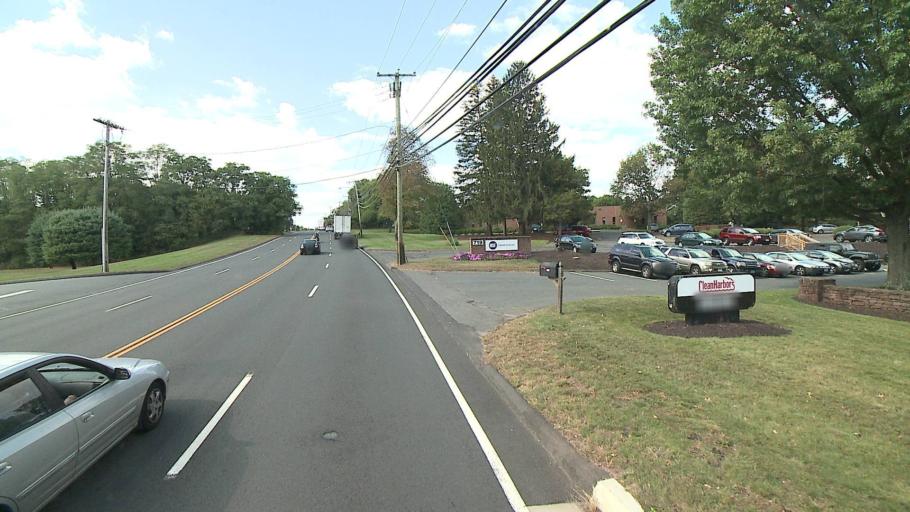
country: US
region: Connecticut
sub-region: Hartford County
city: Bristol
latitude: 41.6523
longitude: -72.9080
